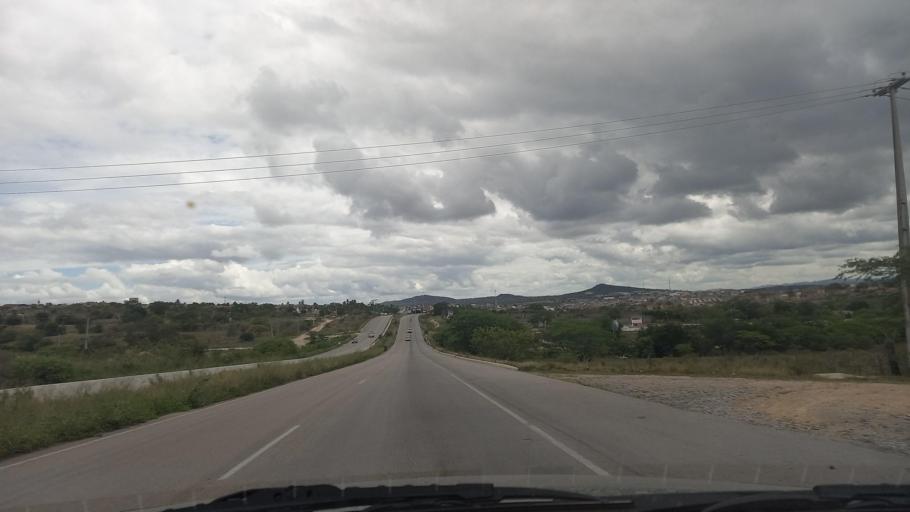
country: BR
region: Pernambuco
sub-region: Caruaru
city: Caruaru
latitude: -8.3270
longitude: -36.1164
